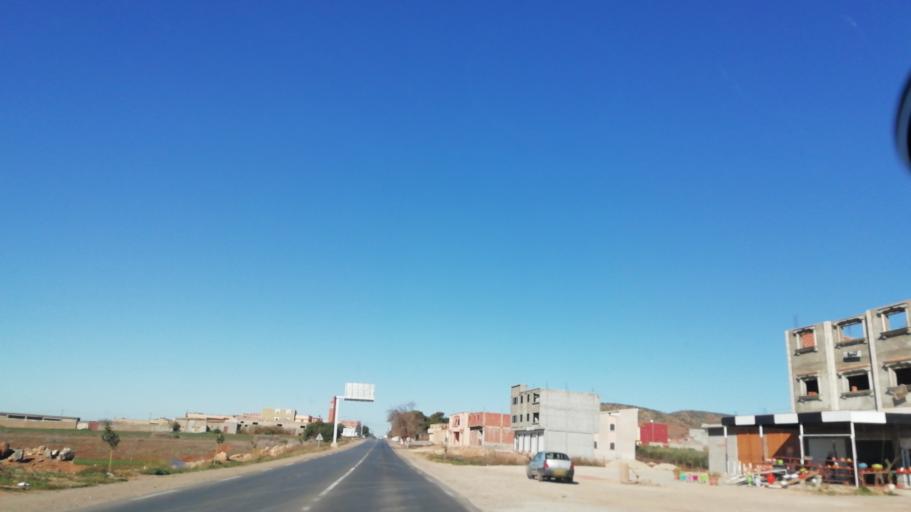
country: DZ
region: Tlemcen
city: Nedroma
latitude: 34.8830
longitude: -1.9024
